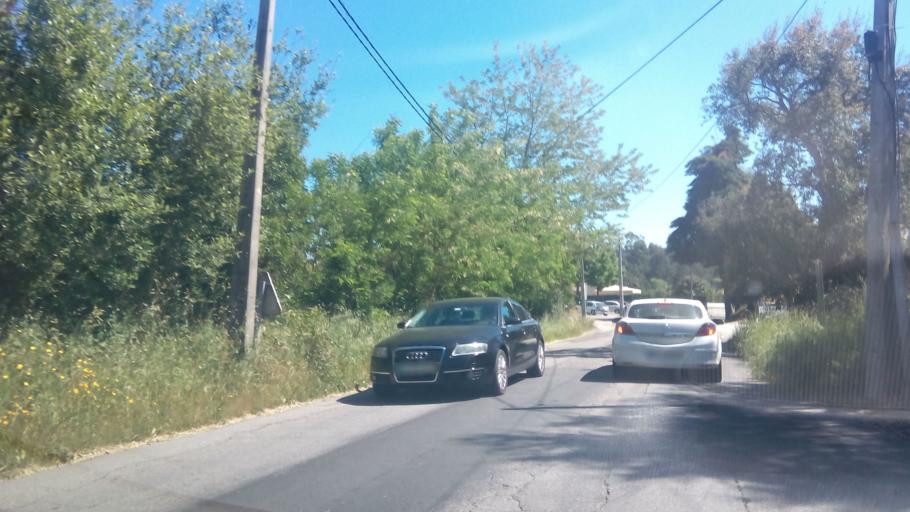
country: PT
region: Porto
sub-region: Paredes
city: Baltar
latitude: 41.1825
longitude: -8.3549
